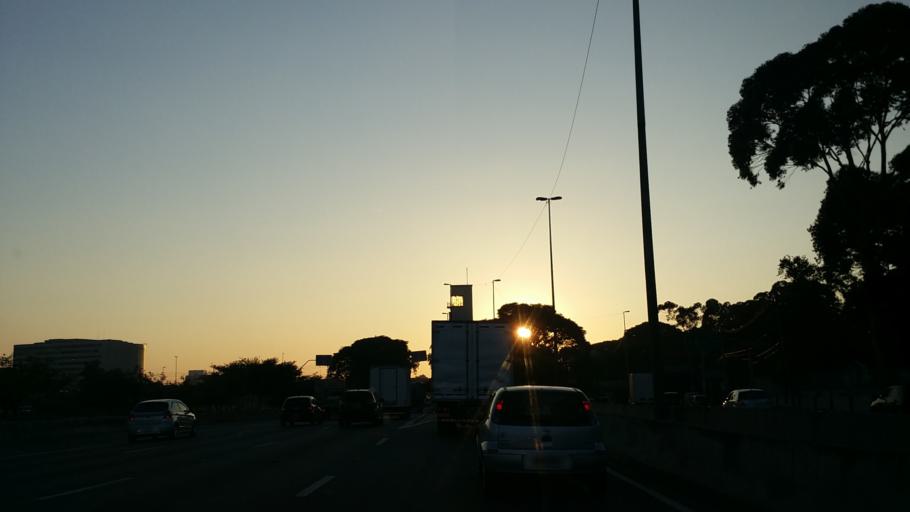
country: BR
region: Sao Paulo
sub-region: Sao Paulo
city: Sao Paulo
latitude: -23.5196
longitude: -46.6322
